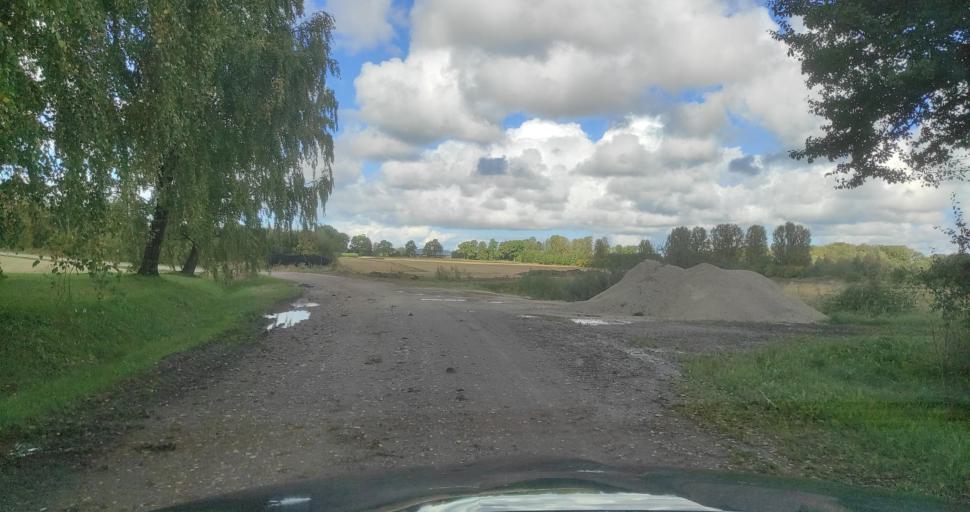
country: LV
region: Ventspils Rajons
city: Piltene
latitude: 57.2703
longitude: 21.5880
